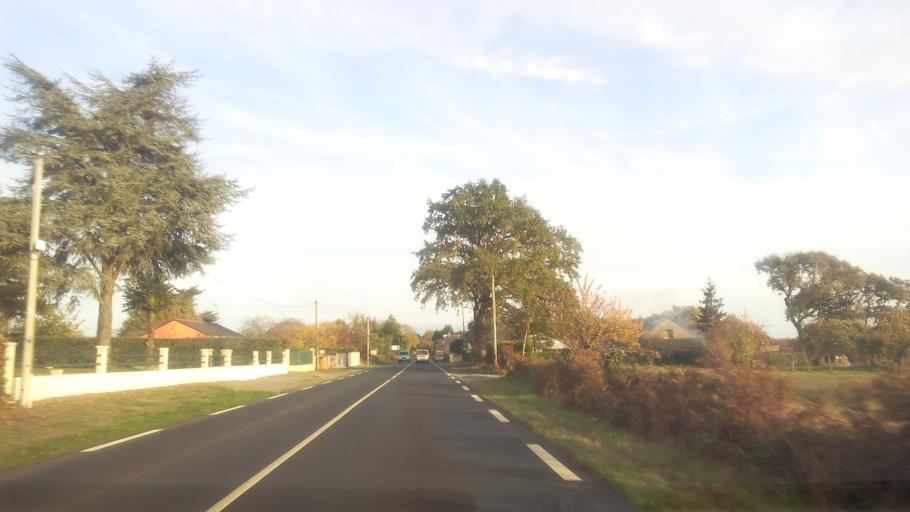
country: FR
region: Pays de la Loire
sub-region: Departement de la Loire-Atlantique
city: Saint-Nicolas-de-Redon
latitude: 47.6416
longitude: -2.0283
